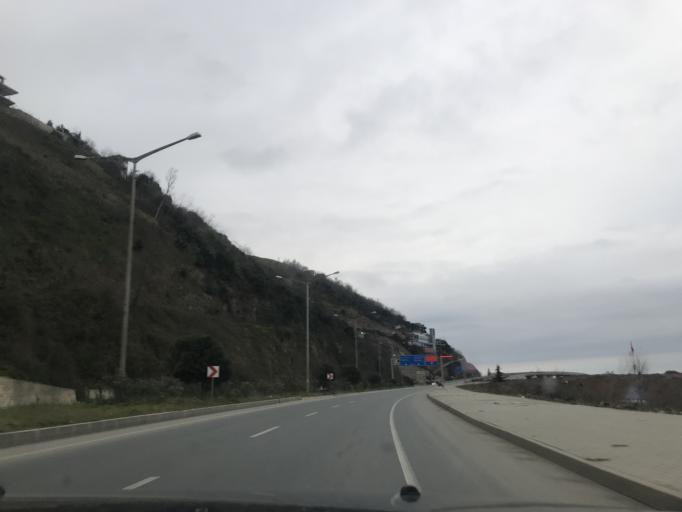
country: TR
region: Trabzon
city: Derecik
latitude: 40.9987
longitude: 39.6408
